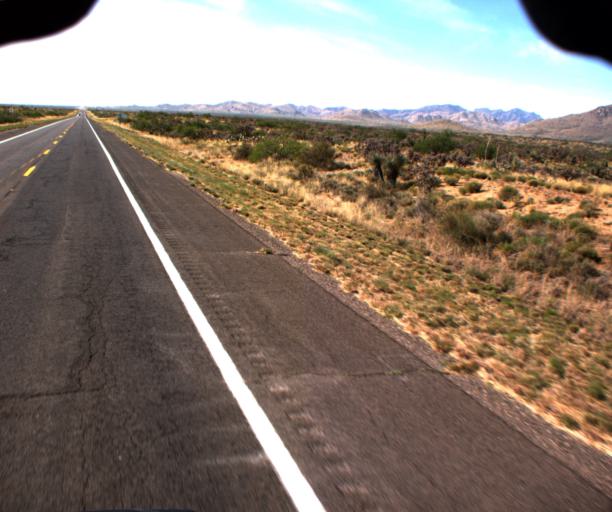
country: US
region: Arizona
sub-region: Graham County
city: Swift Trail Junction
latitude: 32.6223
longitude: -109.6893
